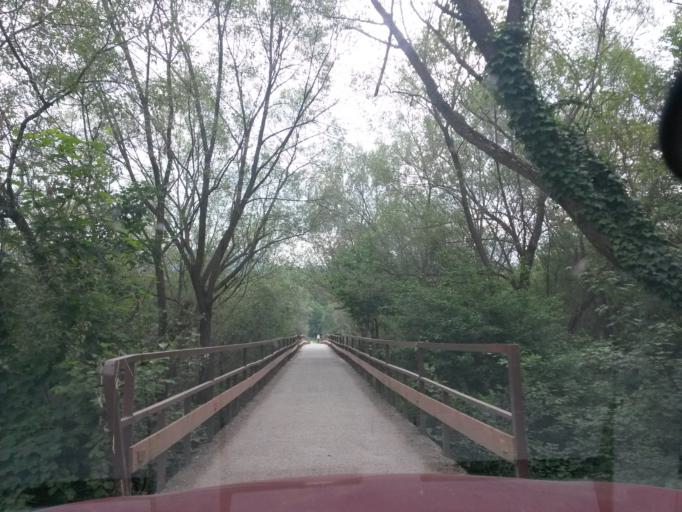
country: UA
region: Zakarpattia
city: Velykyi Bereznyi
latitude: 48.9078
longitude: 22.4663
